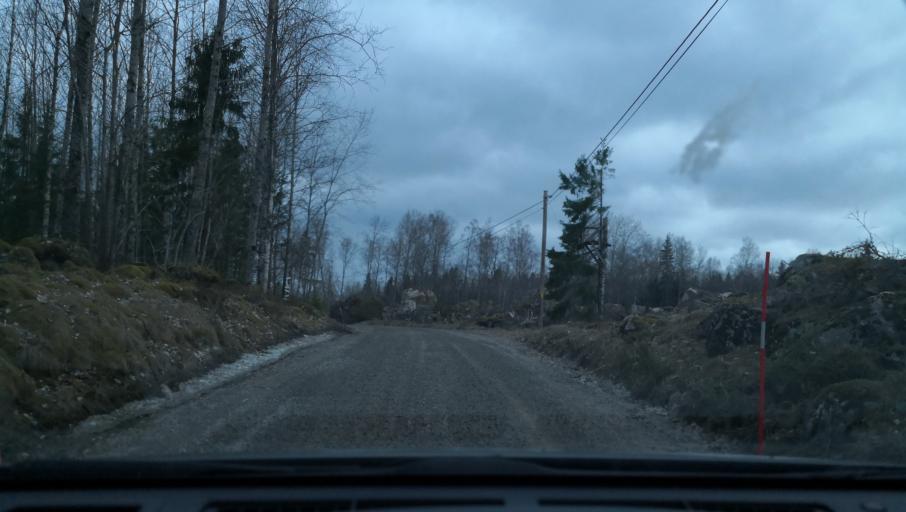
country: SE
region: OErebro
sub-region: Lindesbergs Kommun
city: Fellingsbro
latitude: 59.5997
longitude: 15.6354
